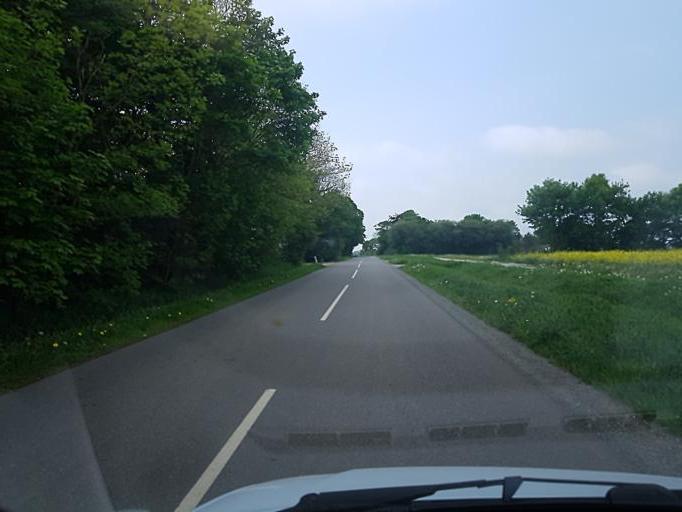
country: DK
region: South Denmark
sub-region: Varde Kommune
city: Varde
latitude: 55.5389
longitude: 8.5094
